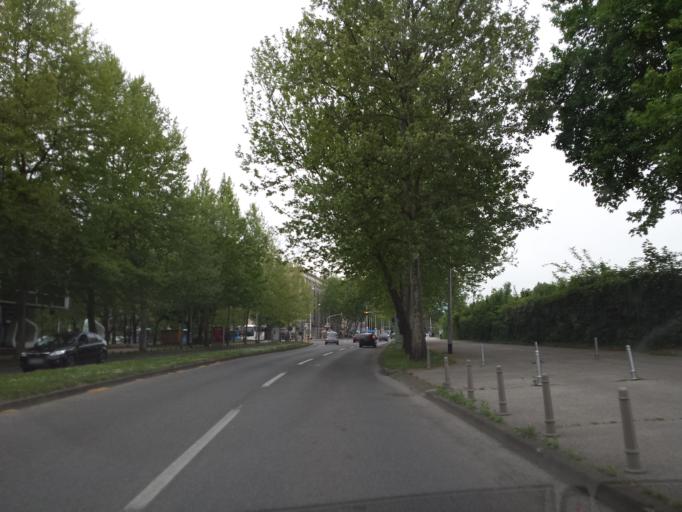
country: HR
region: Grad Zagreb
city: Zagreb
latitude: 45.8161
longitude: 16.0131
